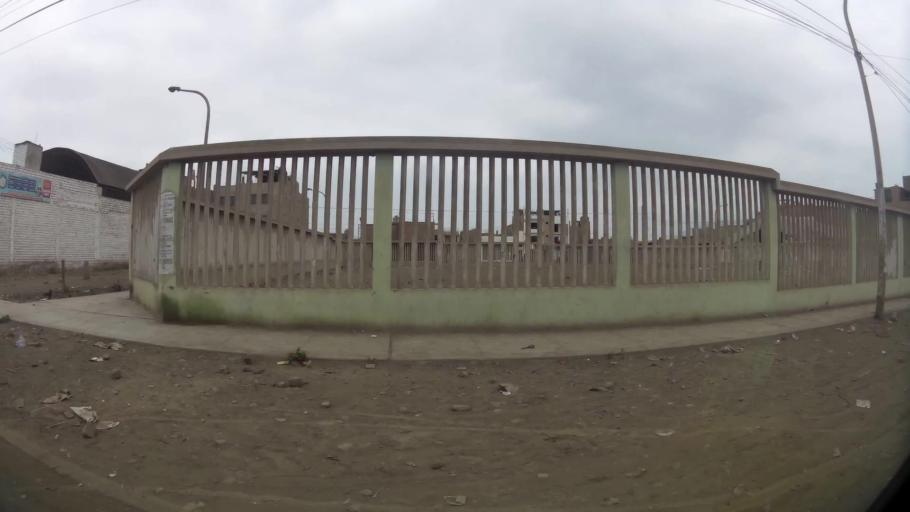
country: PE
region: Lima
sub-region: Provincia de Huaral
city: Huaral
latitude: -11.4954
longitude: -77.1990
